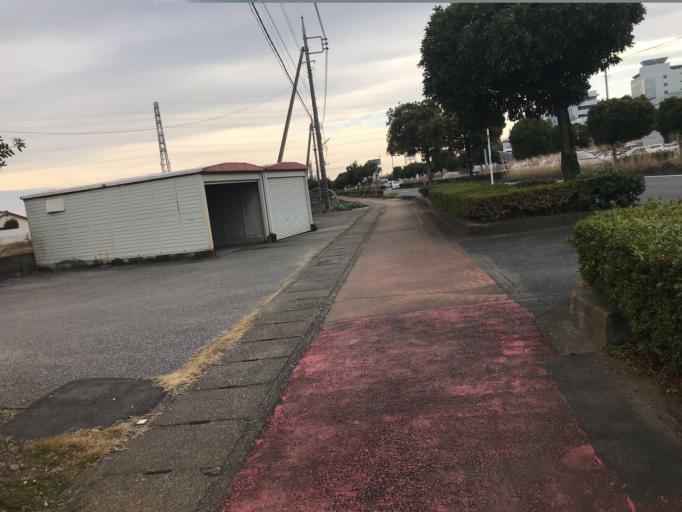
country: JP
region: Gunma
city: Ota
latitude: 36.3119
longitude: 139.3941
